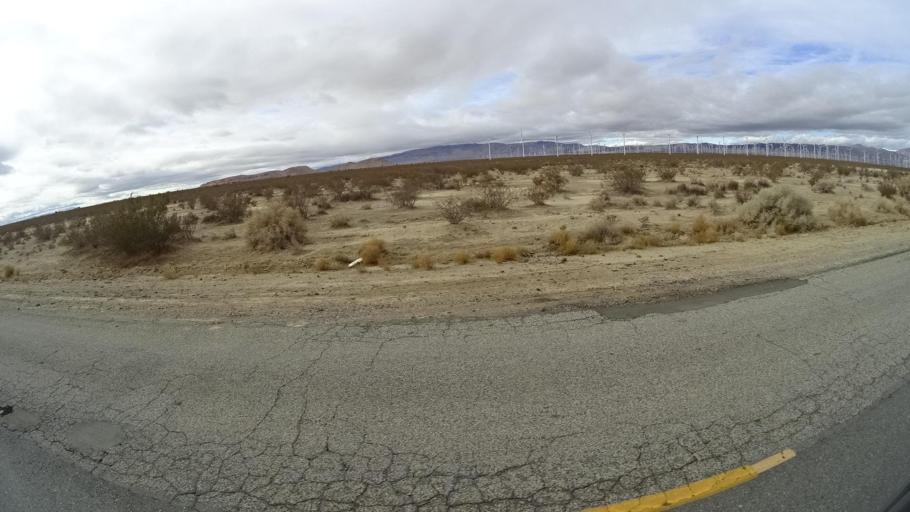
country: US
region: California
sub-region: Kern County
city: Mojave
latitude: 34.9777
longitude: -118.2096
